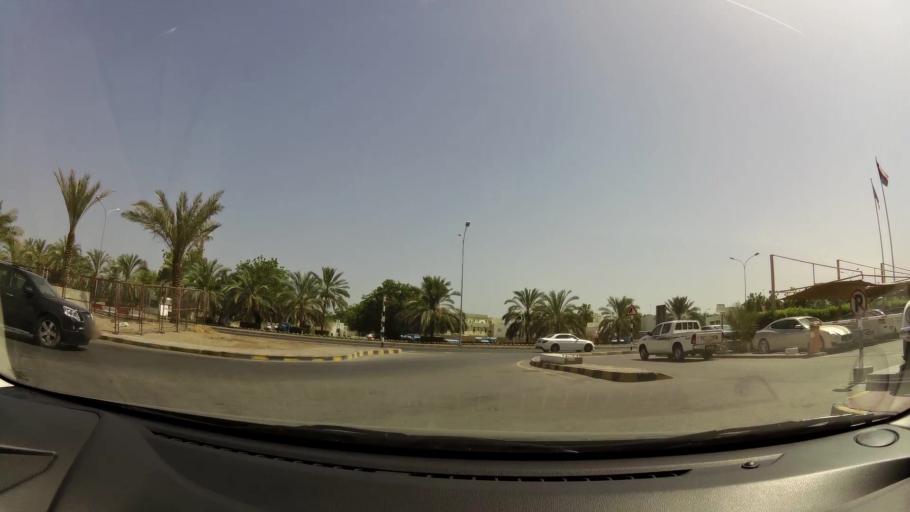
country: OM
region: Muhafazat Masqat
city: Bawshar
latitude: 23.5969
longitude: 58.4457
